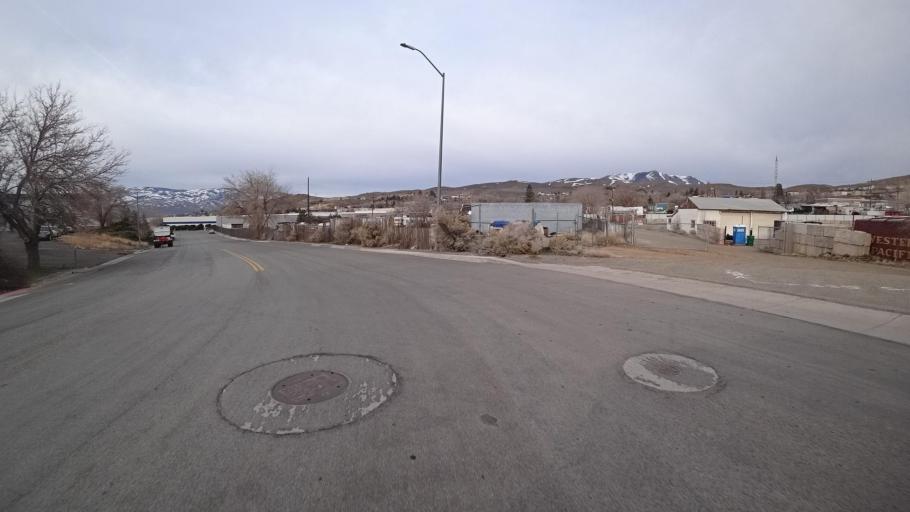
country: US
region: Nevada
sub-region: Washoe County
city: Reno
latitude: 39.5722
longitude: -119.8185
